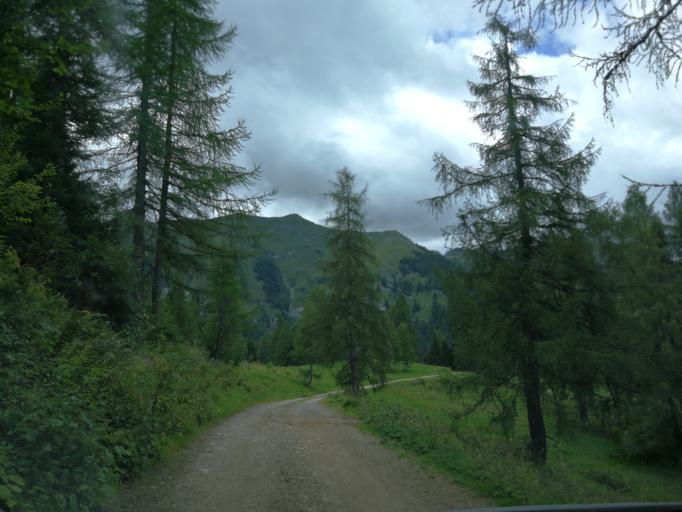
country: IT
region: Trentino-Alto Adige
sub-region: Provincia di Trento
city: Castel Condino
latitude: 45.9385
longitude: 10.5503
